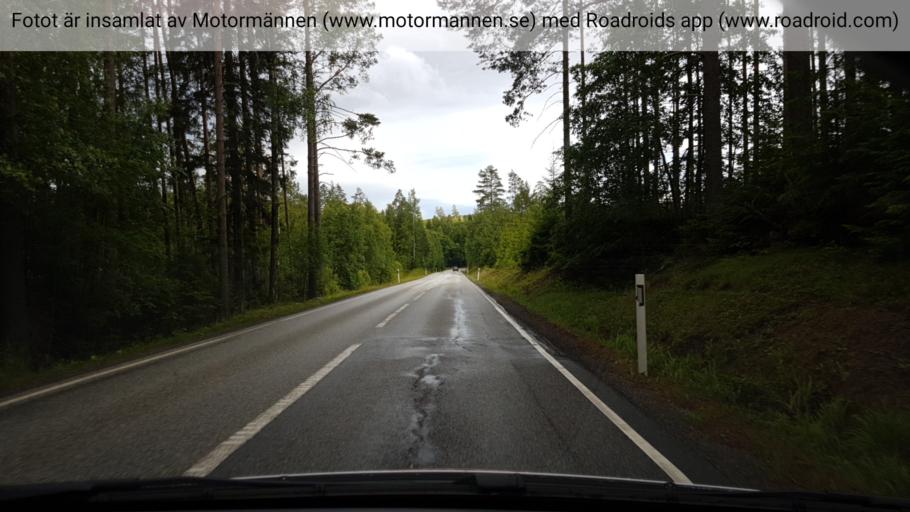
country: SE
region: OErebro
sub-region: Ljusnarsbergs Kommun
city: Kopparberg
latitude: 59.8471
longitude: 14.9980
